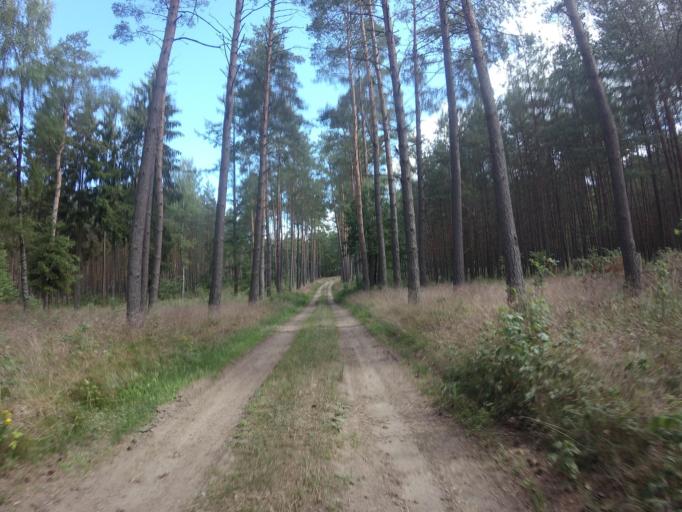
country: PL
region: West Pomeranian Voivodeship
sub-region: Powiat choszczenski
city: Drawno
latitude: 53.2563
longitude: 15.6607
